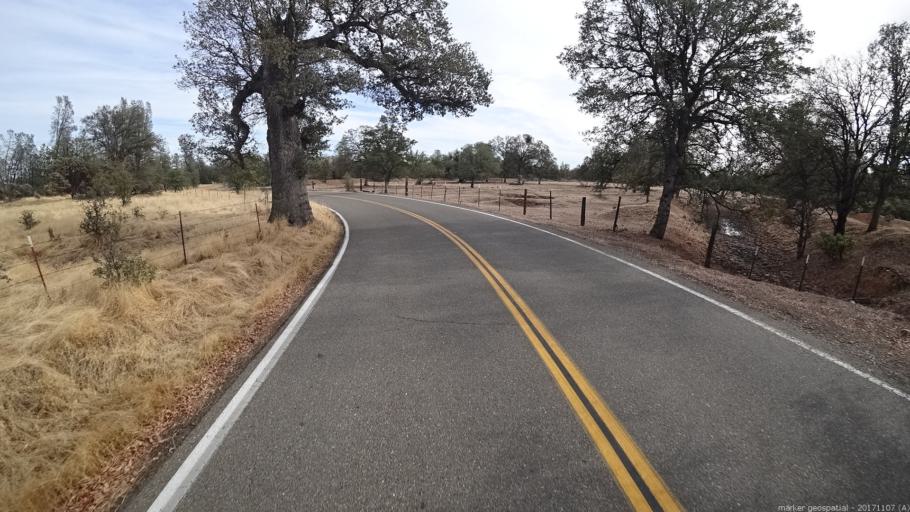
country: US
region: California
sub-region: Shasta County
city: Shasta
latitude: 40.5041
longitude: -122.5328
